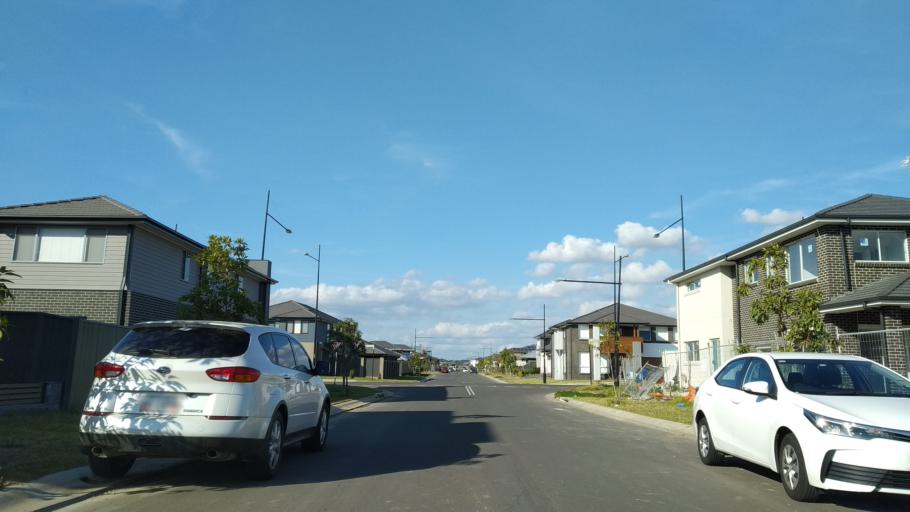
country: AU
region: New South Wales
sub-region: Blacktown
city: Blackett
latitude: -33.6925
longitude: 150.8097
